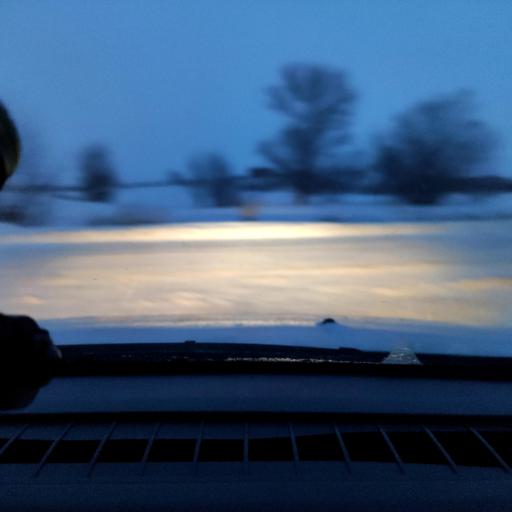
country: RU
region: Samara
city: Kinel'-Cherkassy
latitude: 53.4475
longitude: 51.5341
